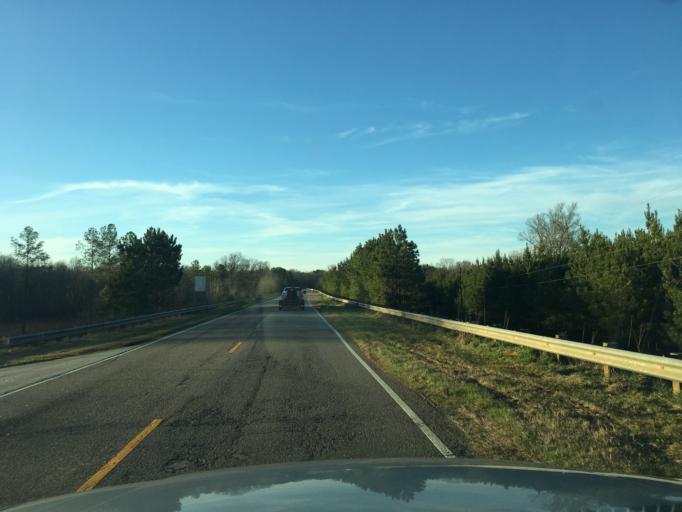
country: US
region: South Carolina
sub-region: Greenwood County
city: Ninety Six
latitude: 34.1712
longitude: -81.8614
